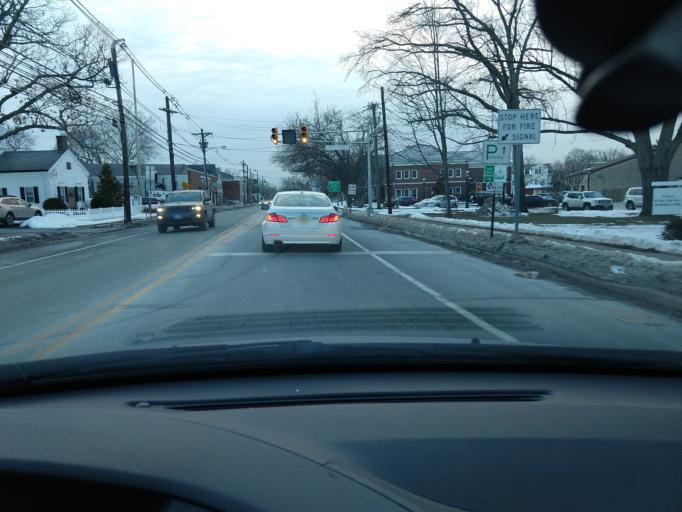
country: US
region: New Jersey
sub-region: Middlesex County
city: Metuchen
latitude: 40.5446
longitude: -74.3613
